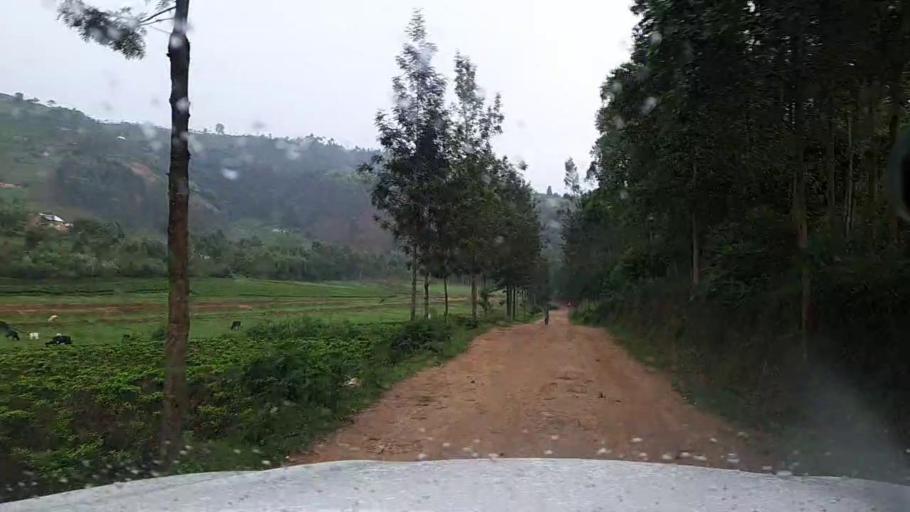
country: RW
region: Northern Province
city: Byumba
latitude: -1.6516
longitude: 29.9275
